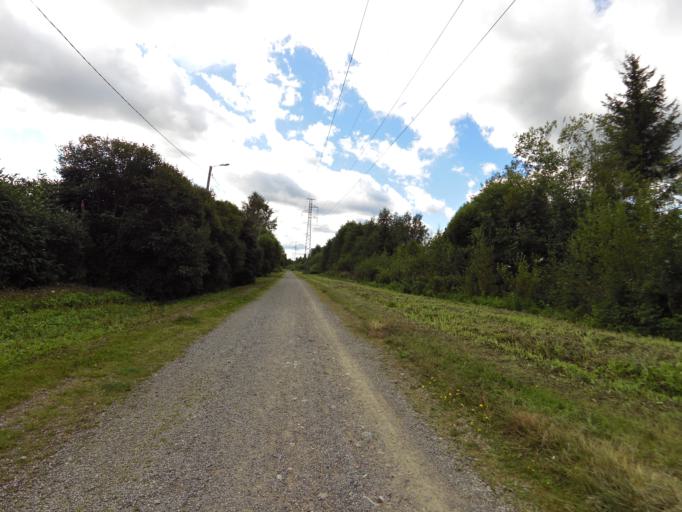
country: FI
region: Pirkanmaa
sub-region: Tampere
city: Yloejaervi
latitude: 61.5132
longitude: 23.6106
